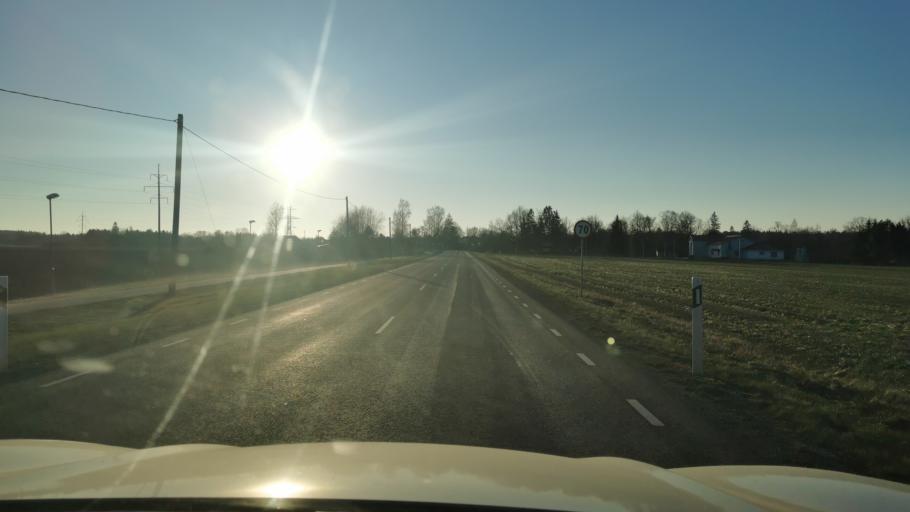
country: EE
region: Ida-Virumaa
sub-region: Kivioli linn
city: Kivioli
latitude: 59.3246
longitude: 27.0113
